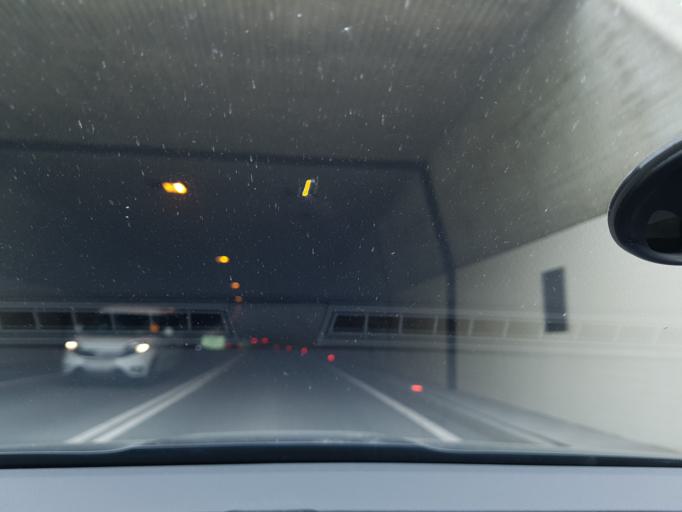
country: AT
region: Tyrol
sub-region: Politischer Bezirk Schwaz
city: Ried im Zillertal
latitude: 47.2988
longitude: 11.8770
